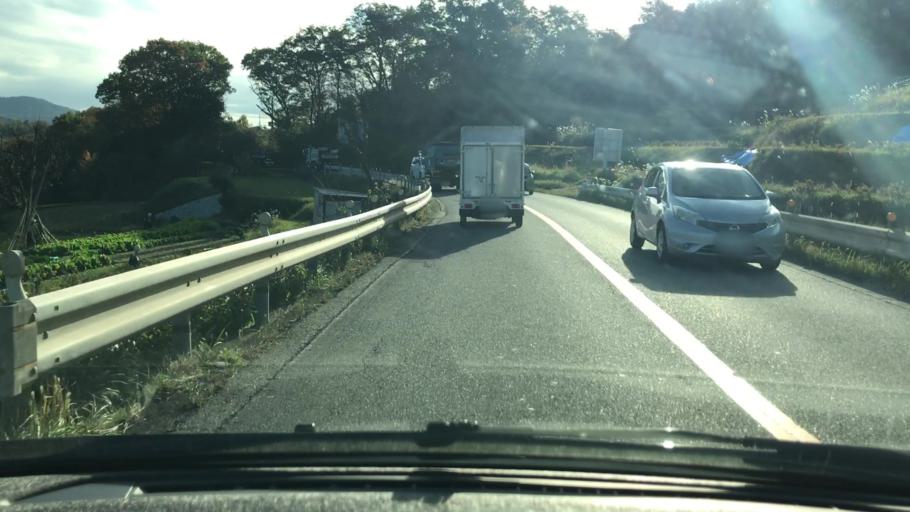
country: JP
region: Hyogo
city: Sandacho
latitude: 34.8334
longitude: 135.2751
